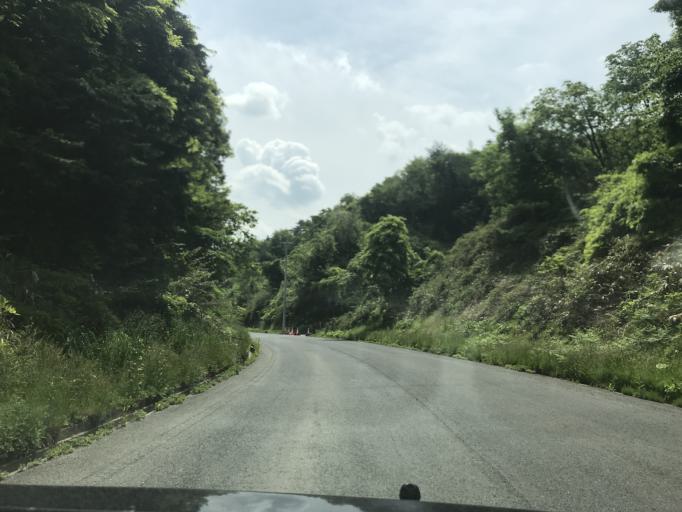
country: JP
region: Iwate
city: Ichinoseki
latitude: 38.8596
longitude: 140.9840
